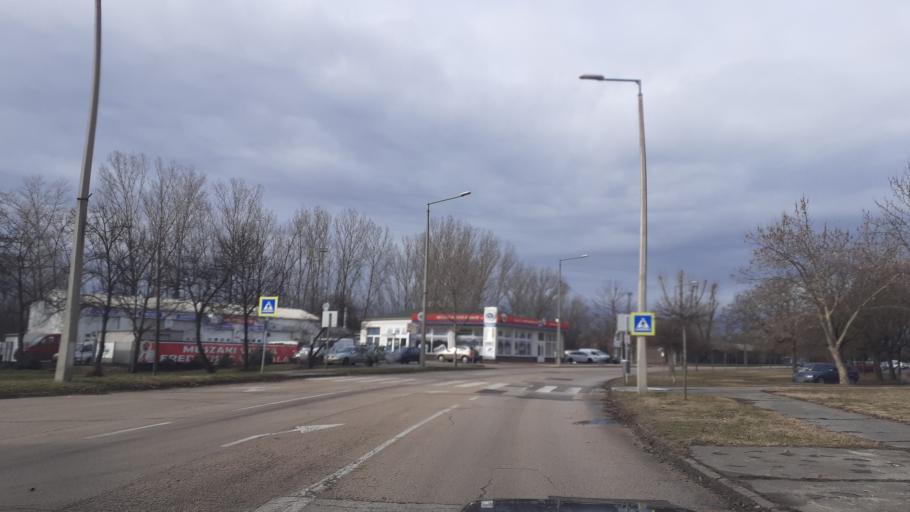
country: HU
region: Fejer
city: dunaujvaros
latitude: 46.9606
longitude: 18.9181
